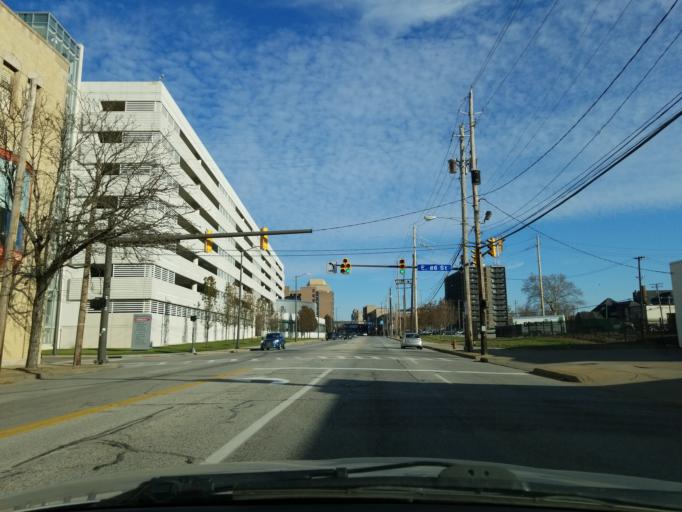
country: US
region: Ohio
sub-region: Cuyahoga County
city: Bratenahl
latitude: 41.5011
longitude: -81.6274
